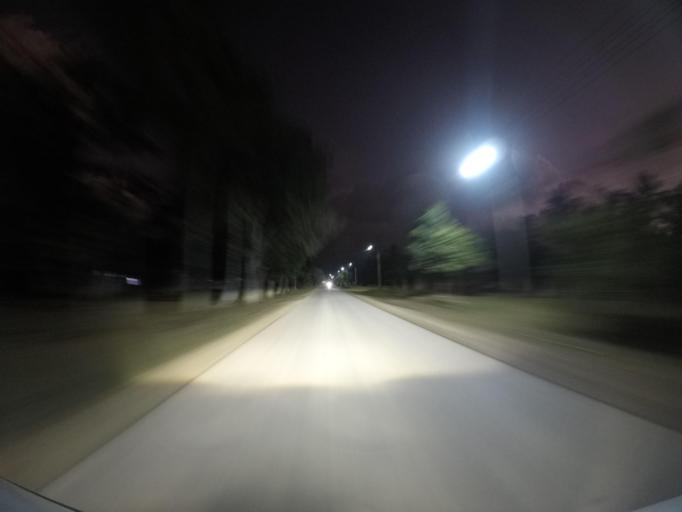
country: TL
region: Lautem
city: Lospalos
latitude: -8.4725
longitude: 126.9930
